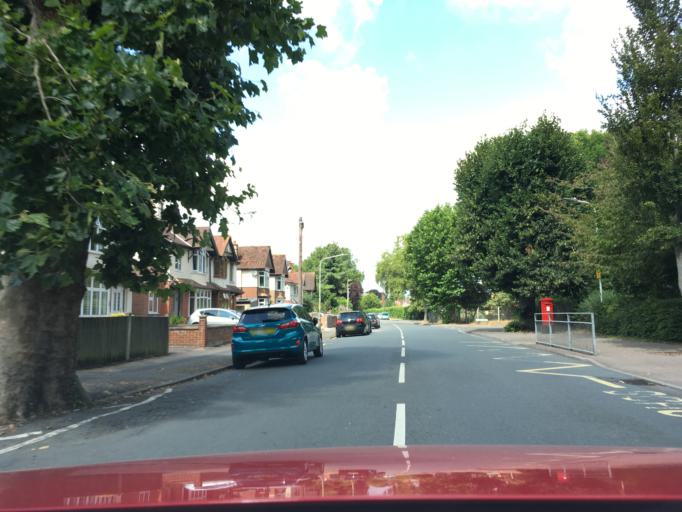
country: GB
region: England
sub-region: Gloucestershire
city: Gloucester
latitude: 51.8725
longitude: -2.2371
